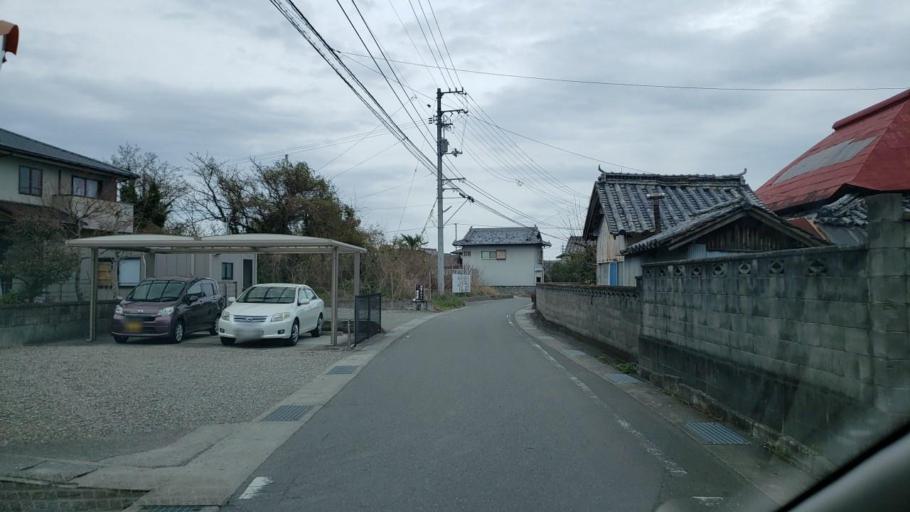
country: JP
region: Tokushima
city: Kamojimacho-jogejima
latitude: 34.0913
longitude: 134.3001
